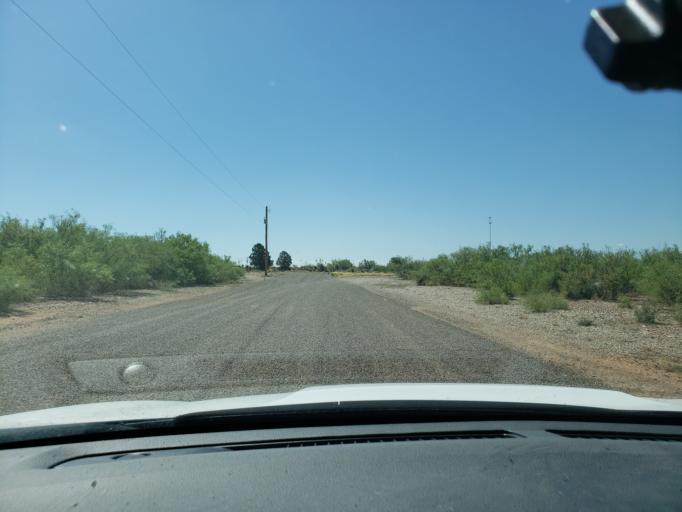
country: US
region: Texas
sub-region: Presidio County
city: Marfa
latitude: 30.5879
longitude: -104.4904
